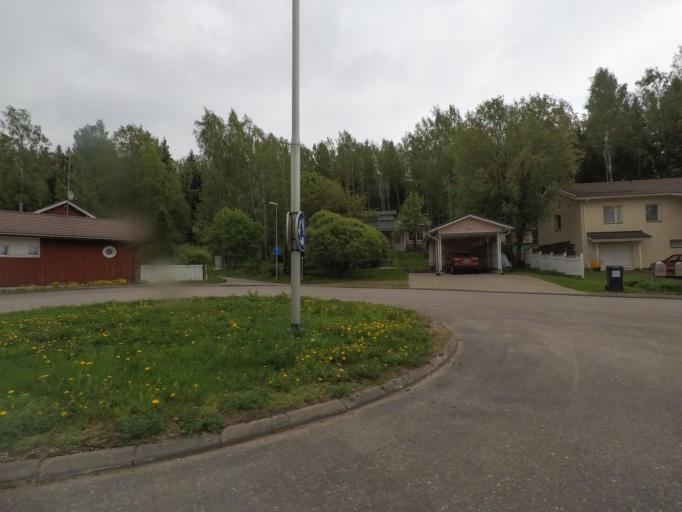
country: FI
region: Uusimaa
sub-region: Helsinki
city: Kirkkonummi
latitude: 60.1278
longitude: 24.4081
